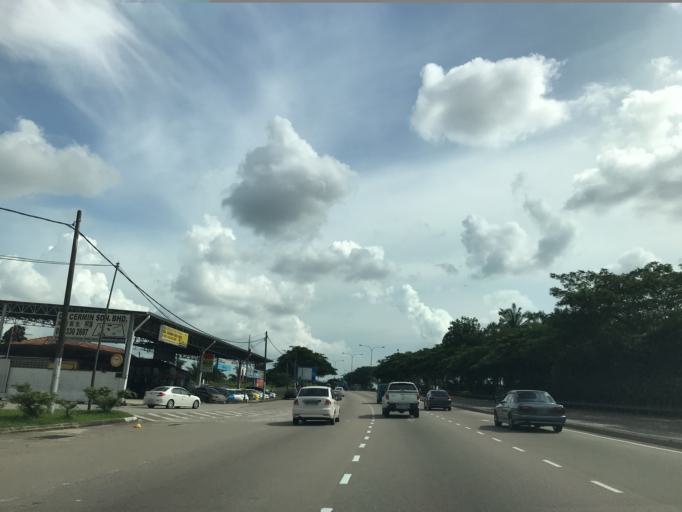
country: MY
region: Johor
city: Taman Senai
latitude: 1.5878
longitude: 103.6484
